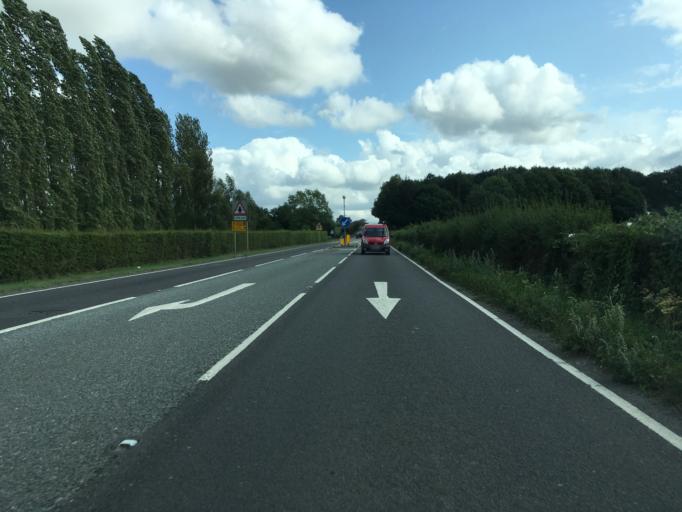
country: GB
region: England
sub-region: Kent
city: Headcorn
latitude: 51.1877
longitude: 0.6059
